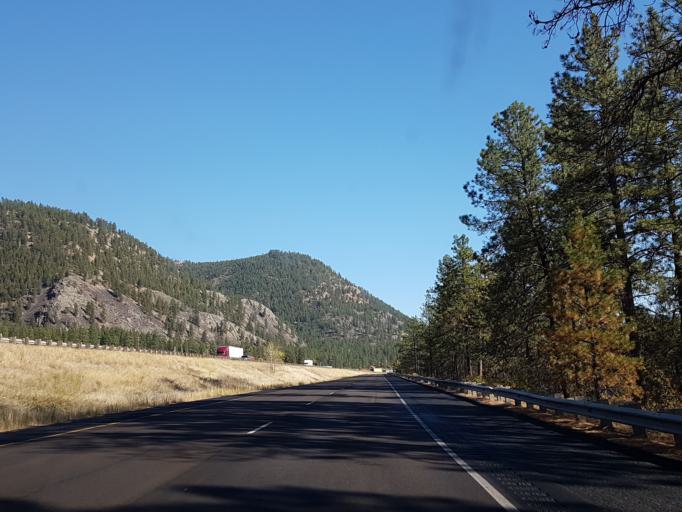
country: US
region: Montana
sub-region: Missoula County
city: Frenchtown
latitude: 47.0202
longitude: -114.5205
